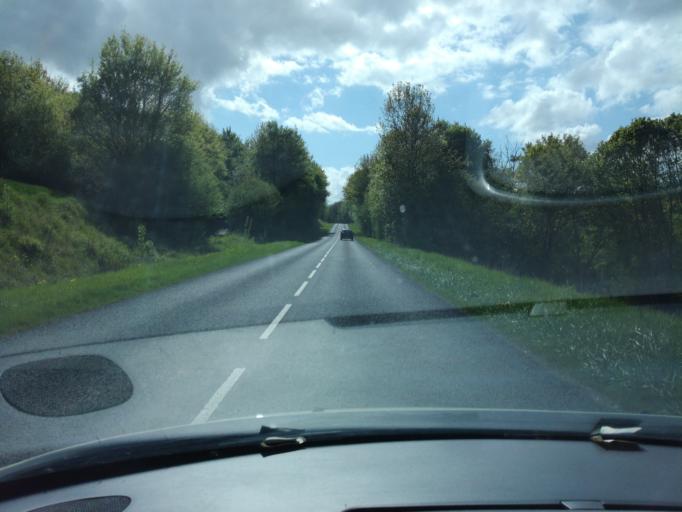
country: FR
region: Picardie
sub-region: Departement de la Somme
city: Picquigny
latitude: 49.8894
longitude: 2.1064
